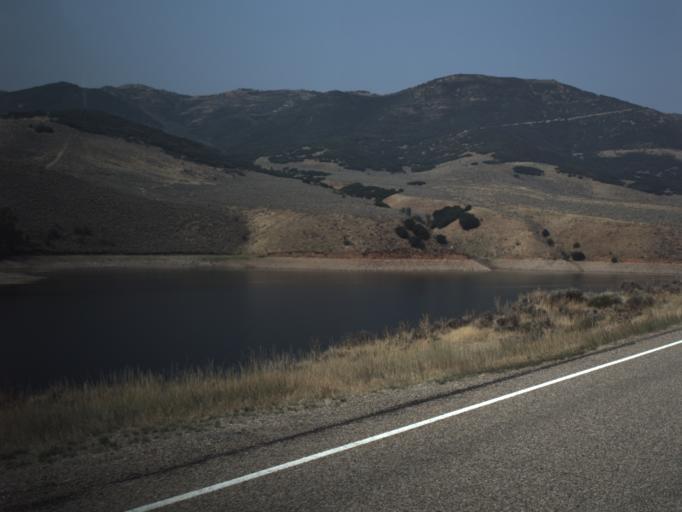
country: US
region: Utah
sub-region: Summit County
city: Summit Park
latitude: 40.8963
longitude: -111.5862
